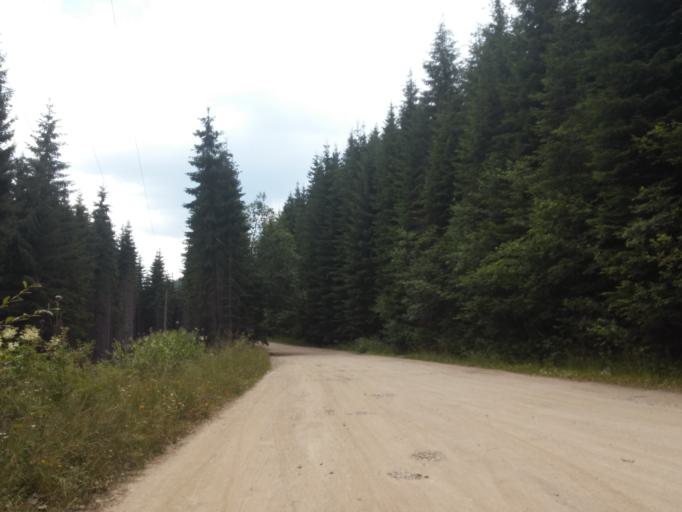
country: RO
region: Valcea
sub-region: Comuna Voineasa
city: Voineasa
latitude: 45.4320
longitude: 23.7580
